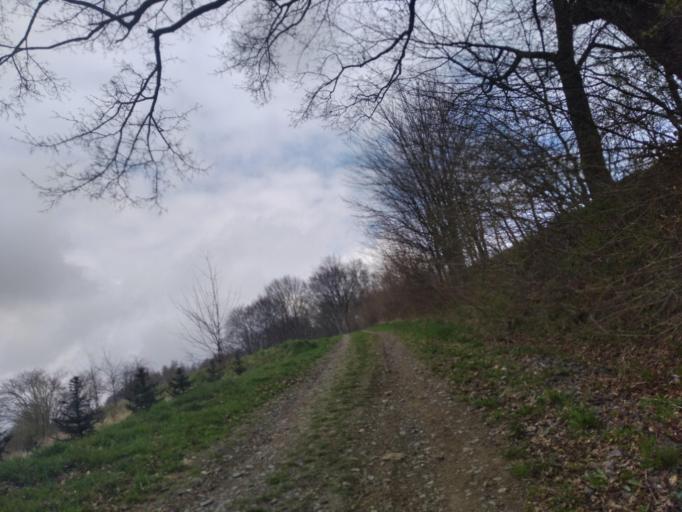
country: PL
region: Subcarpathian Voivodeship
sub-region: Powiat strzyzowski
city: Wisniowa
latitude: 49.8783
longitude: 21.6898
